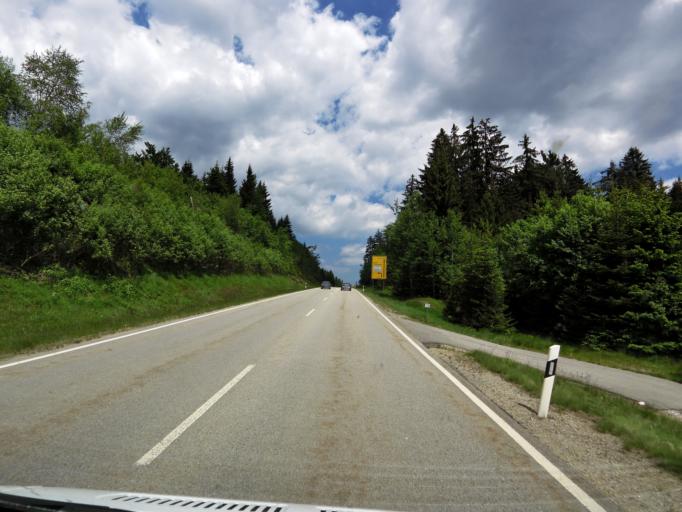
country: DE
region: Bavaria
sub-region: Lower Bavaria
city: Philippsreut
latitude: 48.8677
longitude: 13.6838
